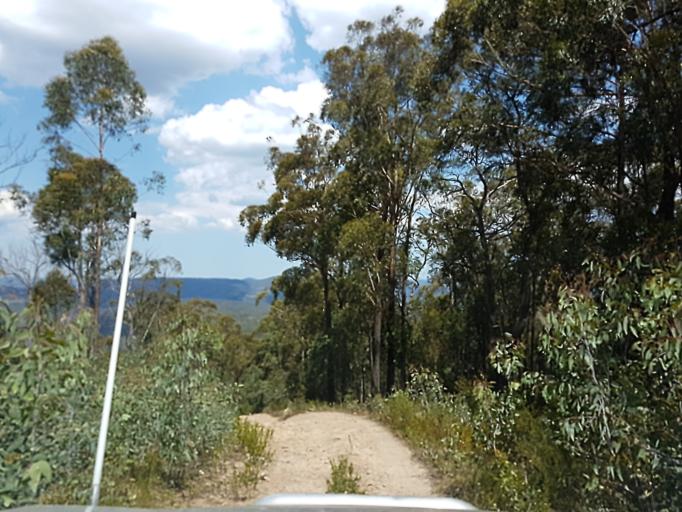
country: AU
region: Victoria
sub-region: East Gippsland
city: Lakes Entrance
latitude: -37.4024
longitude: 148.2989
